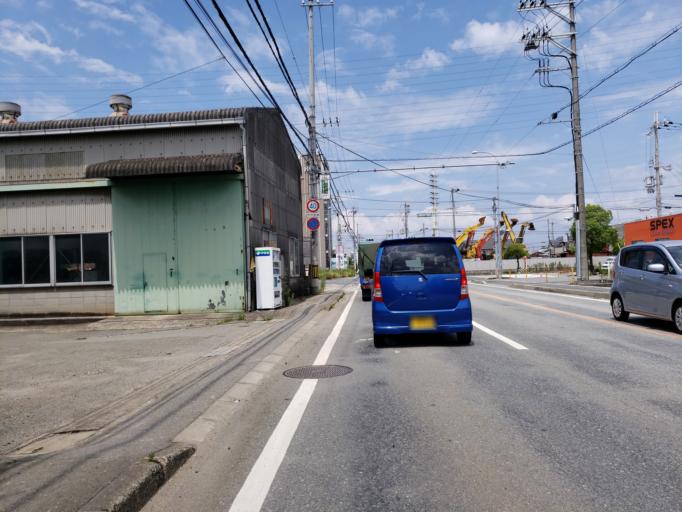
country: JP
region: Hyogo
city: Himeji
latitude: 34.7922
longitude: 134.6863
